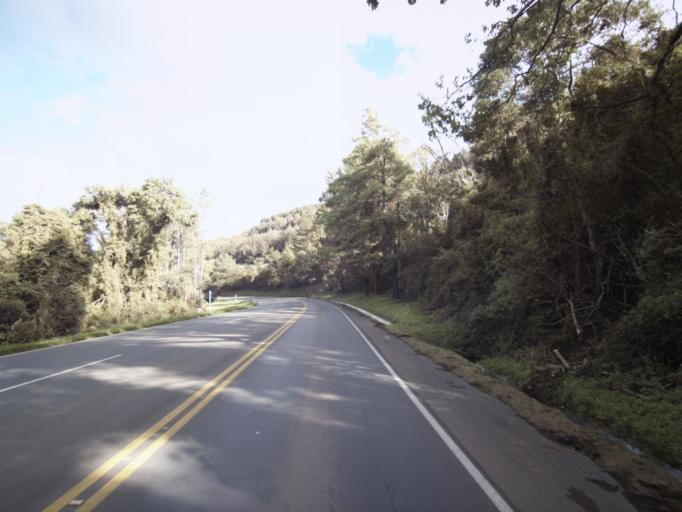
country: BR
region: Santa Catarina
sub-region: Joacaba
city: Joacaba
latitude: -26.9833
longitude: -51.7543
